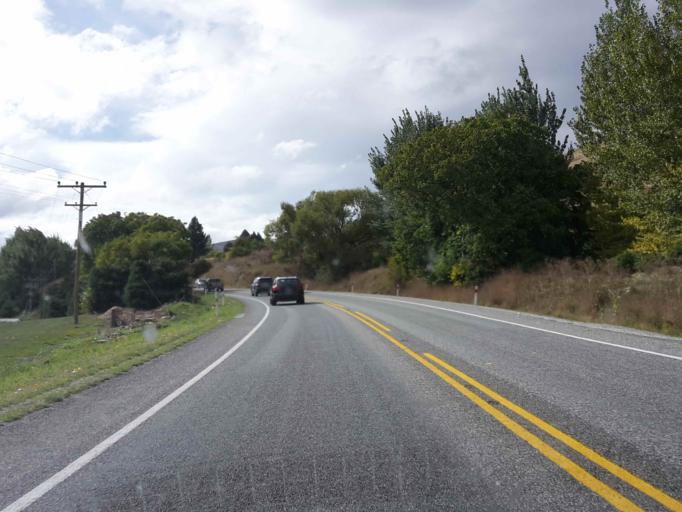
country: NZ
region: Otago
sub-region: Queenstown-Lakes District
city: Arrowtown
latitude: -44.9856
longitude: 168.8187
